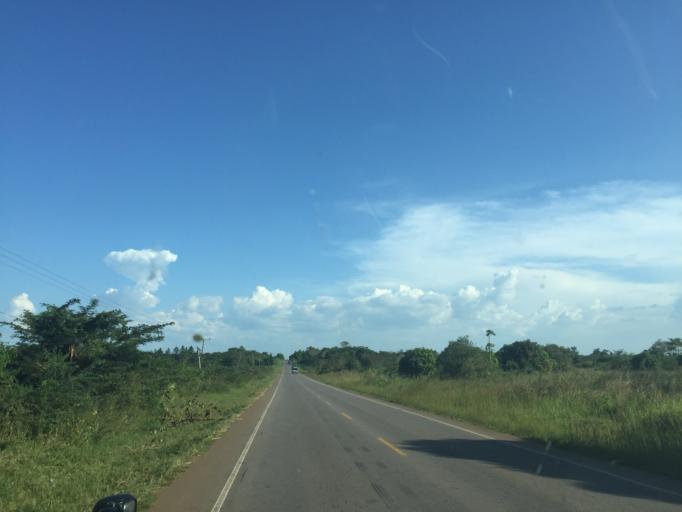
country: UG
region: Central Region
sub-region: Nakasongola District
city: Nakasongola
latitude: 1.2689
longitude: 32.4448
